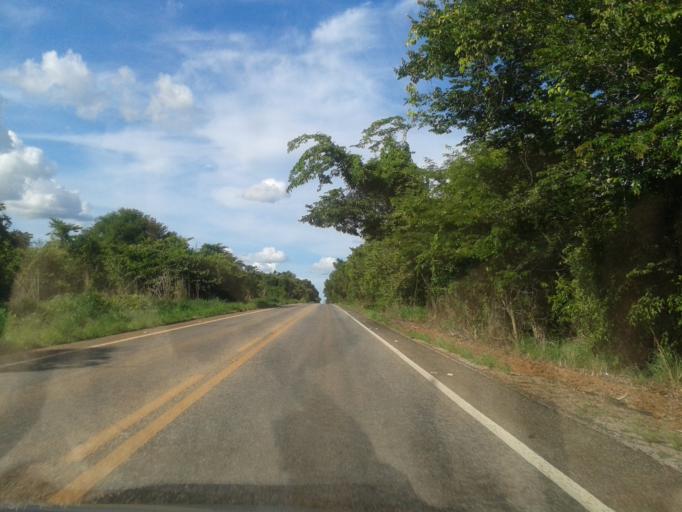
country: BR
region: Goias
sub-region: Mozarlandia
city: Mozarlandia
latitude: -14.4487
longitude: -50.4616
